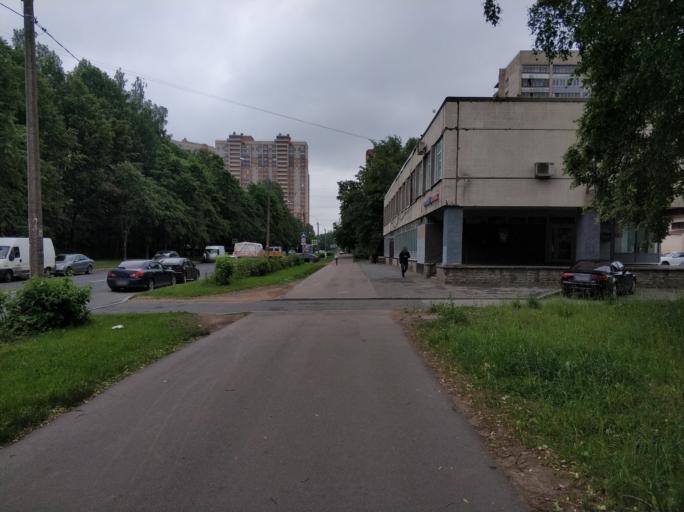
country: RU
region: St.-Petersburg
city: Grazhdanka
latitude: 60.0334
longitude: 30.3968
